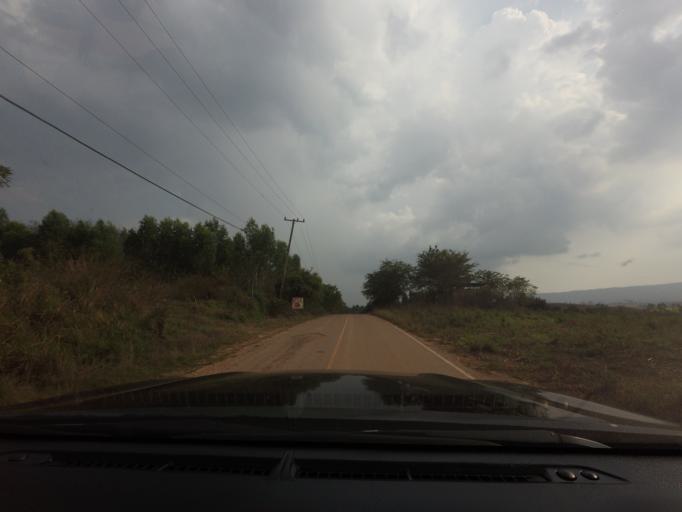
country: TH
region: Nakhon Ratchasima
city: Wang Nam Khiao
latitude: 14.4432
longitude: 101.6912
